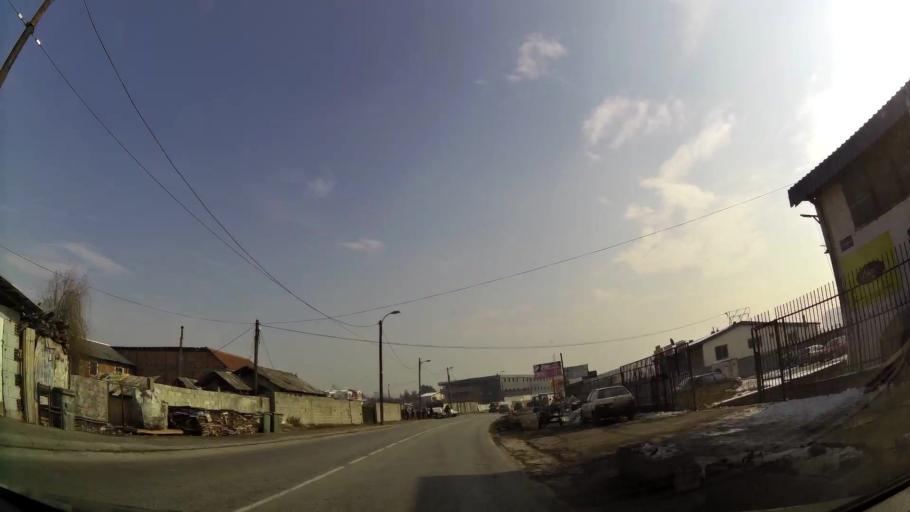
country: MK
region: Suto Orizari
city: Suto Orizare
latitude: 42.0145
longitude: 21.3855
